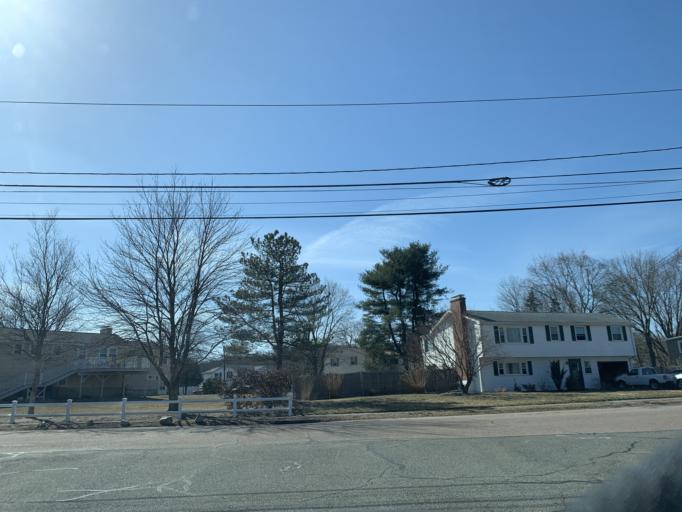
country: US
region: Massachusetts
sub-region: Norfolk County
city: Westwood
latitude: 42.1924
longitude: -71.2238
